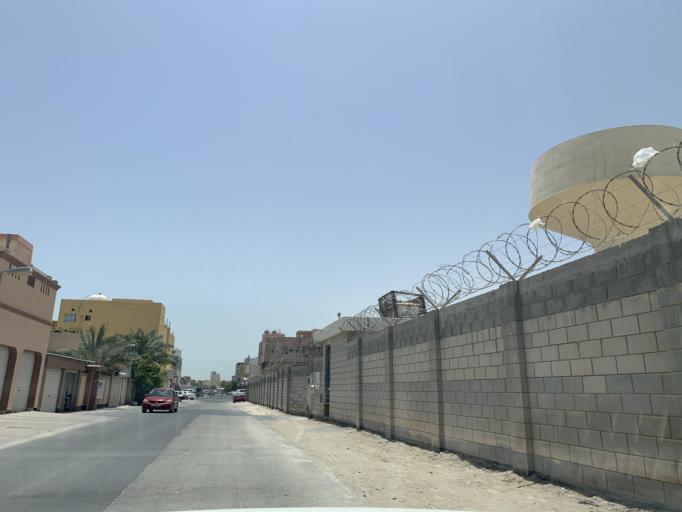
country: BH
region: Northern
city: Sitrah
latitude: 26.1662
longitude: 50.6110
